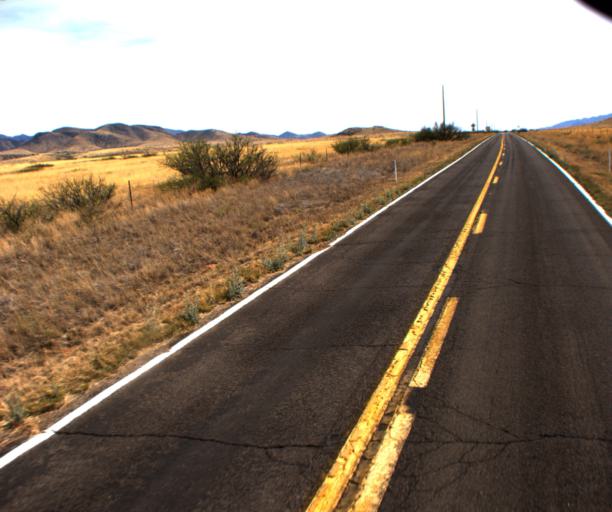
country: US
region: Arizona
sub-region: Cochise County
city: Willcox
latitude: 31.9673
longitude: -109.4770
